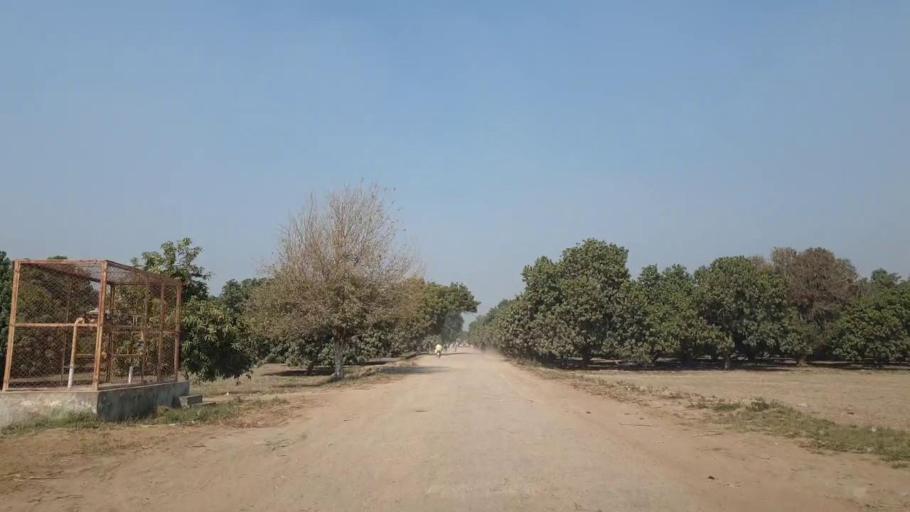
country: PK
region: Sindh
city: Tando Allahyar
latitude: 25.4866
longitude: 68.8226
